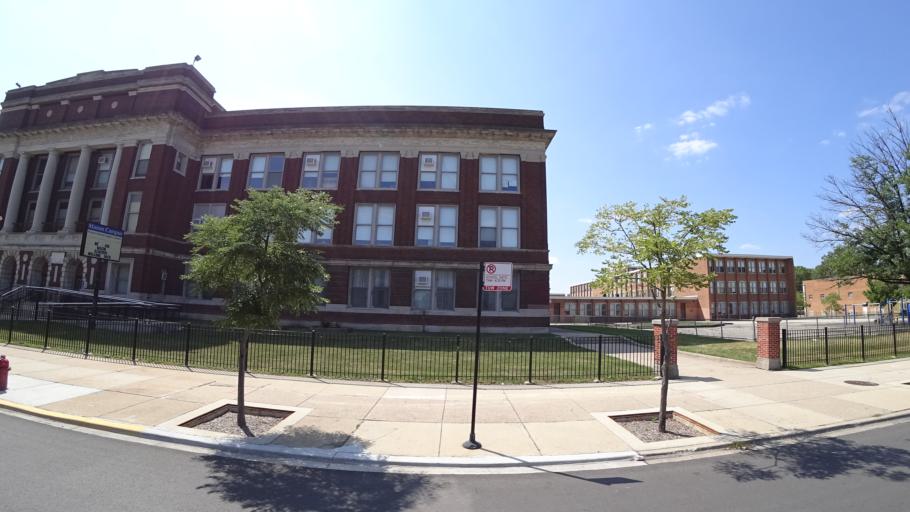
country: US
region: Illinois
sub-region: Cook County
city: Cicero
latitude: 41.8563
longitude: -87.7297
